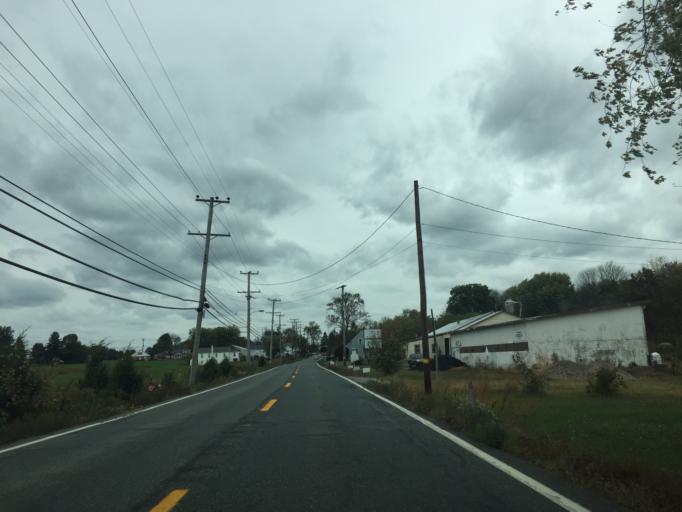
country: US
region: Maryland
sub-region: Harford County
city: Riverside
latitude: 39.5551
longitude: -76.2529
